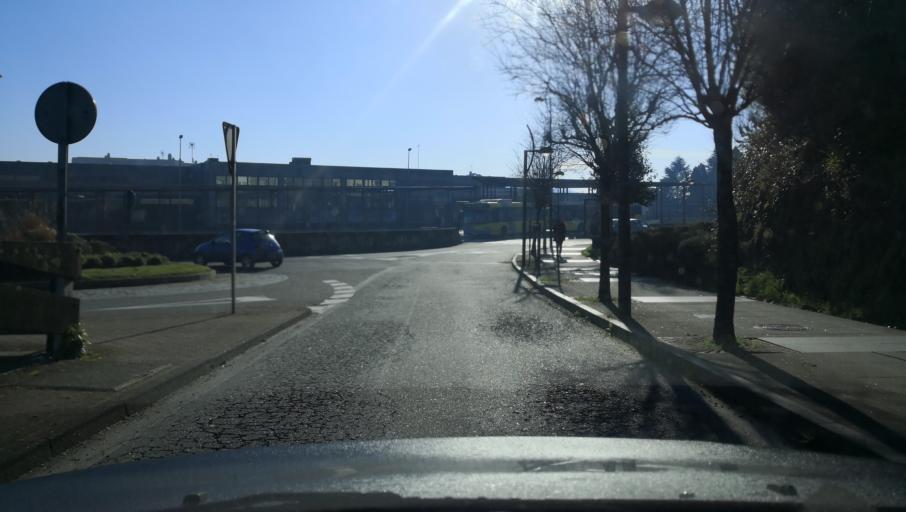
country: ES
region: Galicia
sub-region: Provincia da Coruna
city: Santiago de Compostela
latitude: 42.8877
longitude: -8.5347
